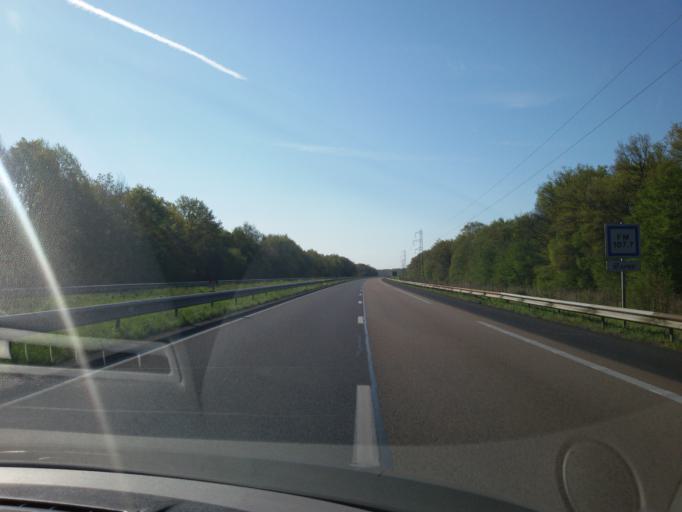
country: FR
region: Centre
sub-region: Departement du Loiret
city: Courtenay
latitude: 48.1000
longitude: 3.0269
